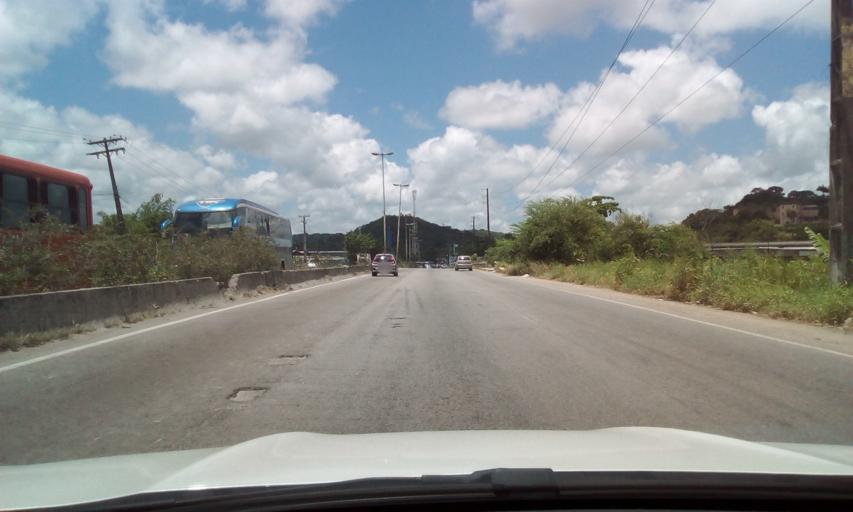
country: BR
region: Pernambuco
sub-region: Recife
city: Recife
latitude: -8.0239
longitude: -34.9428
